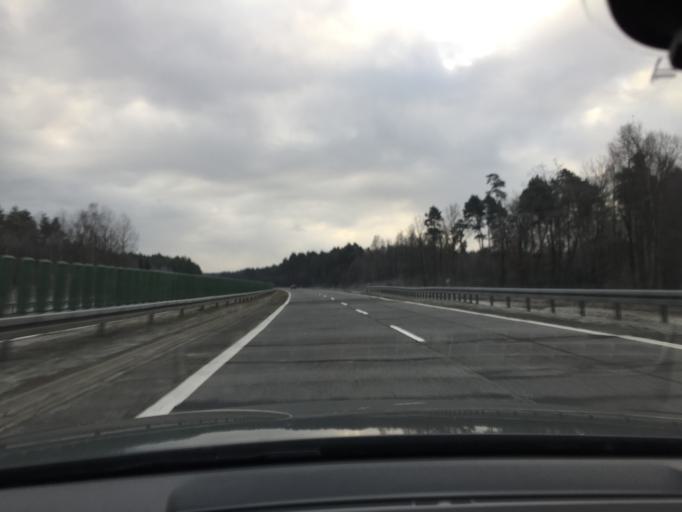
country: PL
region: Lubusz
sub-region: Powiat zarski
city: Trzebiel
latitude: 51.6284
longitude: 14.8810
